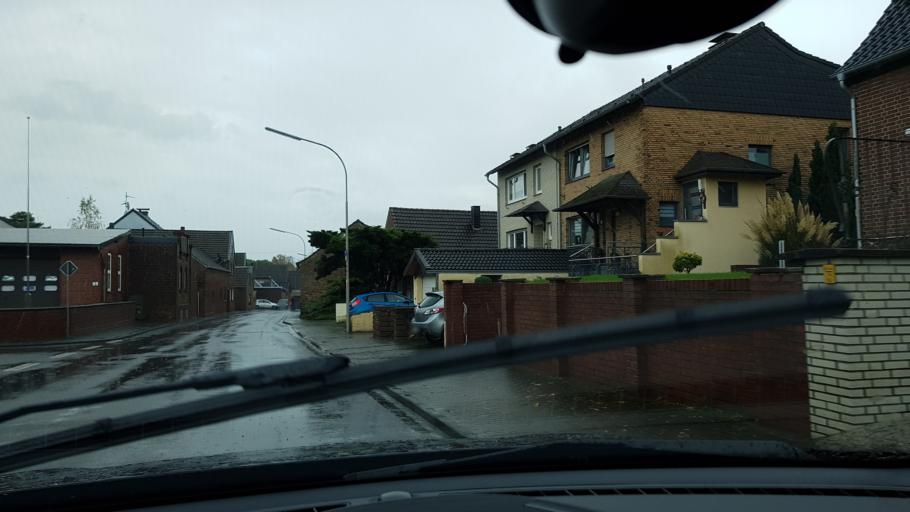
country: DE
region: North Rhine-Westphalia
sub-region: Regierungsbezirk Dusseldorf
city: Rommerskirchen
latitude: 51.0628
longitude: 6.7104
